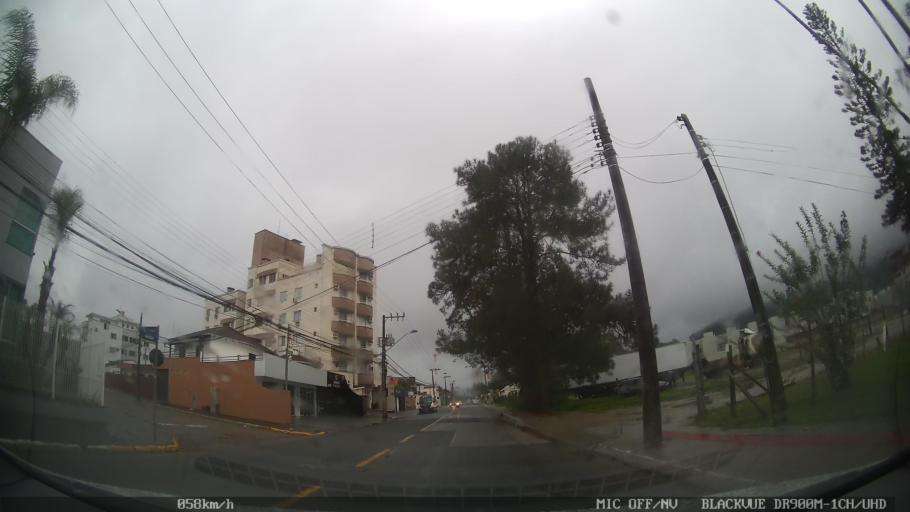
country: BR
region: Santa Catarina
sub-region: Itajai
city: Itajai
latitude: -26.9223
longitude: -48.6793
